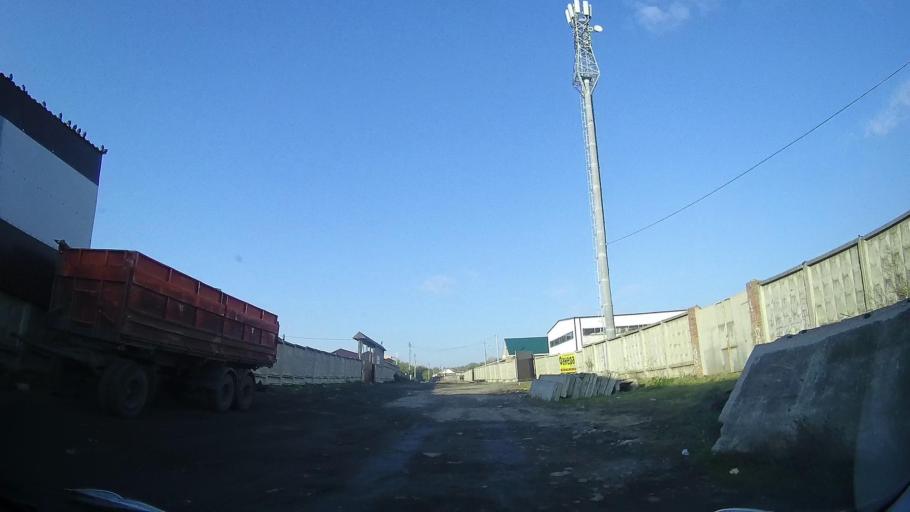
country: RU
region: Rostov
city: Severnyy
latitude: 47.2720
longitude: 39.6755
